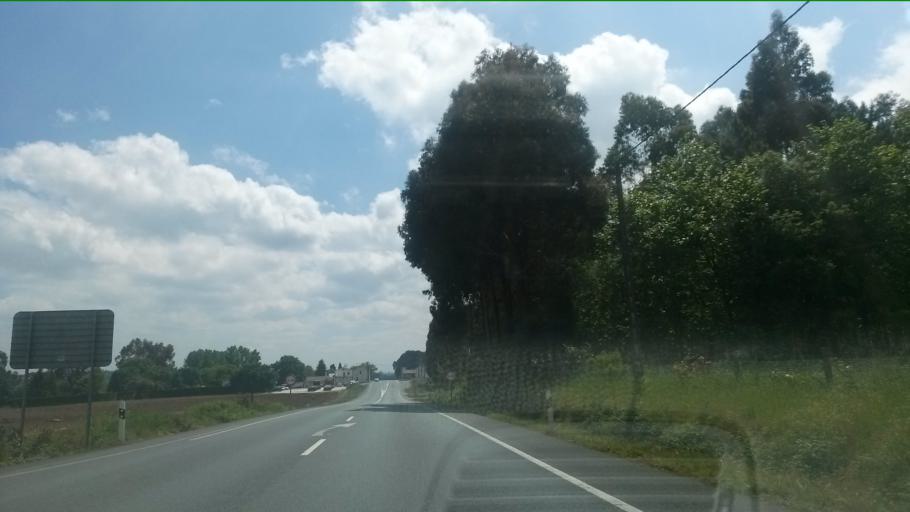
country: ES
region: Galicia
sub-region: Provincia da Coruna
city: Mesia
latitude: 43.0753
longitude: -8.1970
